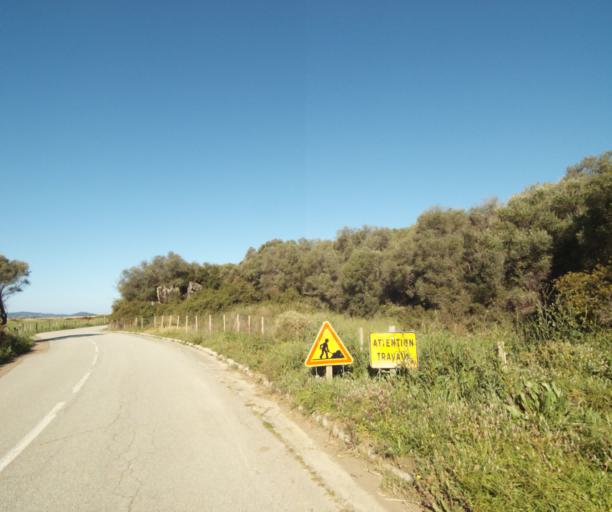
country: FR
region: Corsica
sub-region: Departement de la Corse-du-Sud
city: Propriano
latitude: 41.6650
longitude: 8.8923
